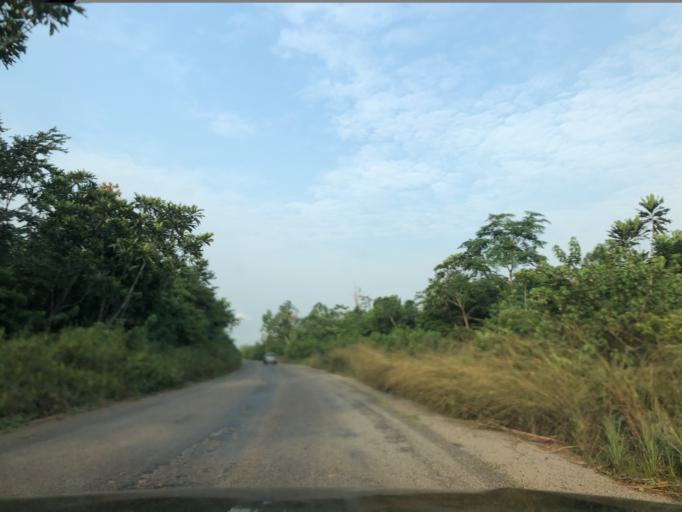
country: CM
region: Littoral
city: Dizangue
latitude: 3.3853
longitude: 10.1071
